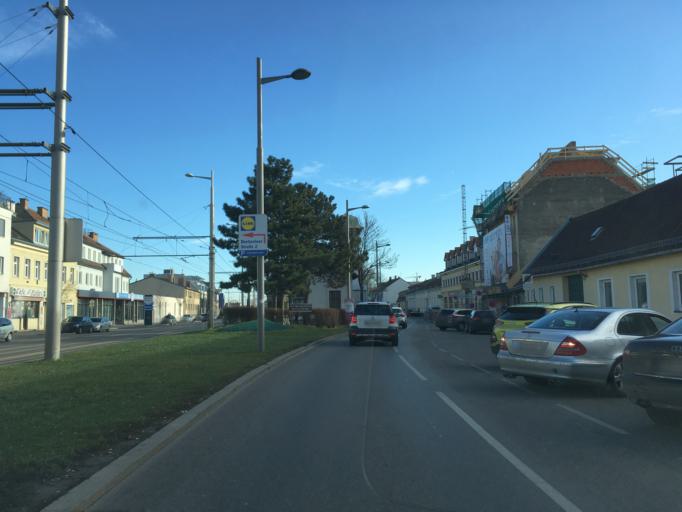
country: AT
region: Lower Austria
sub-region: Politischer Bezirk Wien-Umgebung
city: Gerasdorf bei Wien
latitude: 48.2492
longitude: 16.4464
